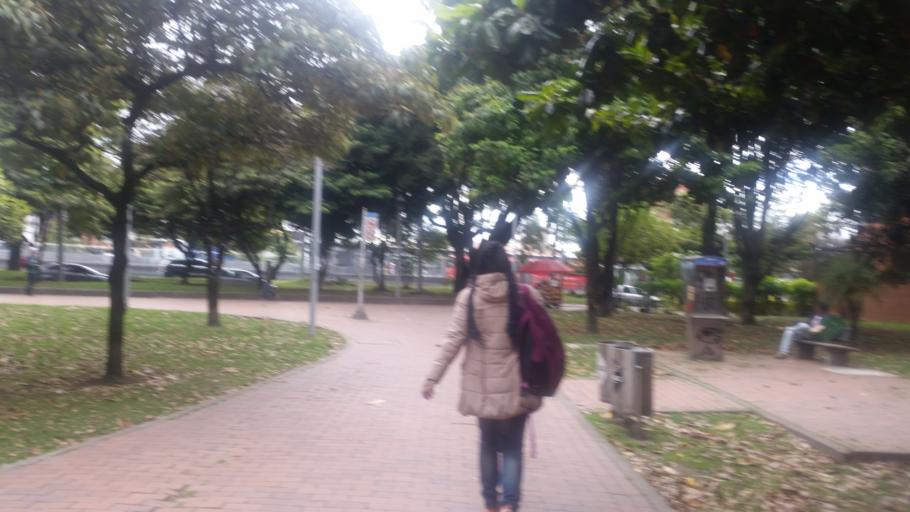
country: CO
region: Bogota D.C.
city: Barrio San Luis
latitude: 4.6756
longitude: -74.0584
